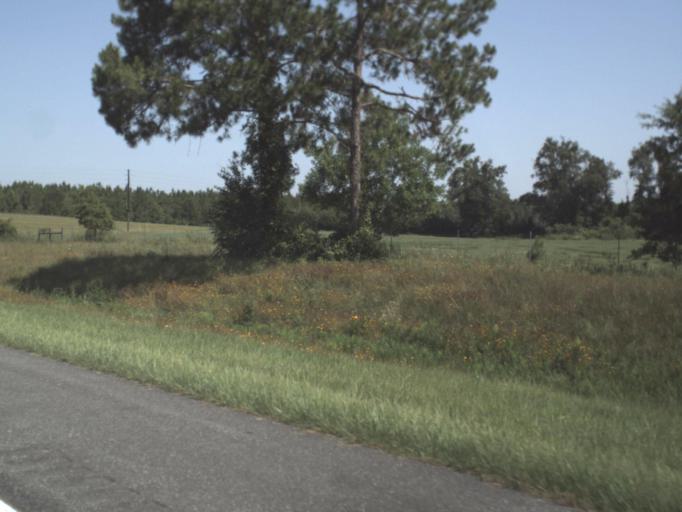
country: US
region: Florida
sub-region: Suwannee County
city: Live Oak
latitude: 30.3428
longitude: -83.1294
